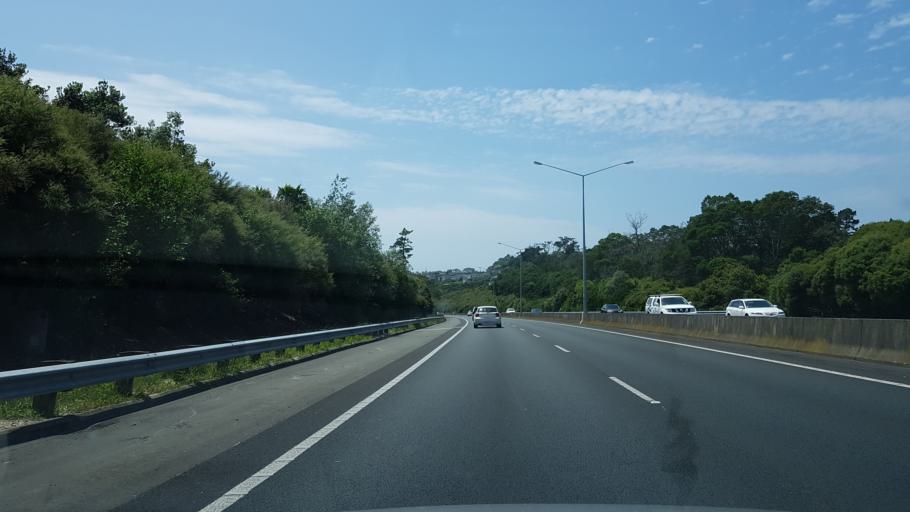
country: NZ
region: Auckland
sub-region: Auckland
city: North Shore
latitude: -36.7778
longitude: 174.6817
